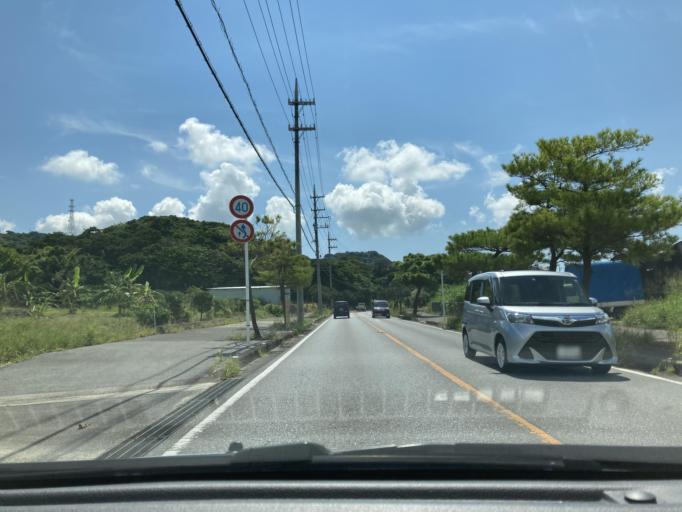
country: JP
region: Okinawa
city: Tomigusuku
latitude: 26.1738
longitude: 127.7520
